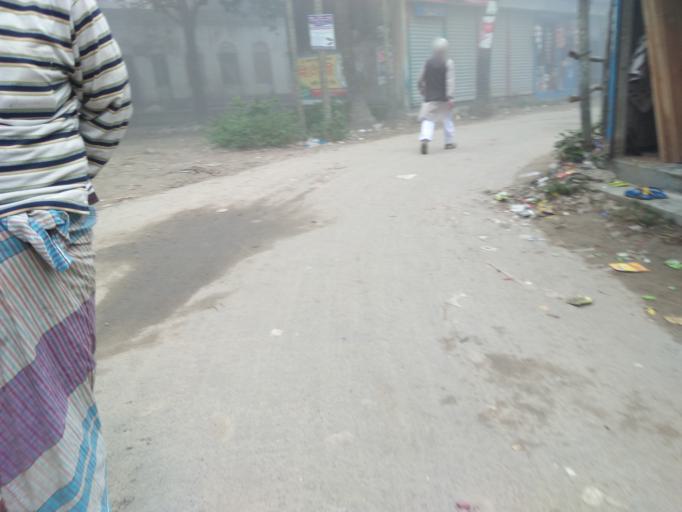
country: BD
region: Dhaka
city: Azimpur
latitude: 23.6900
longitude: 90.3049
